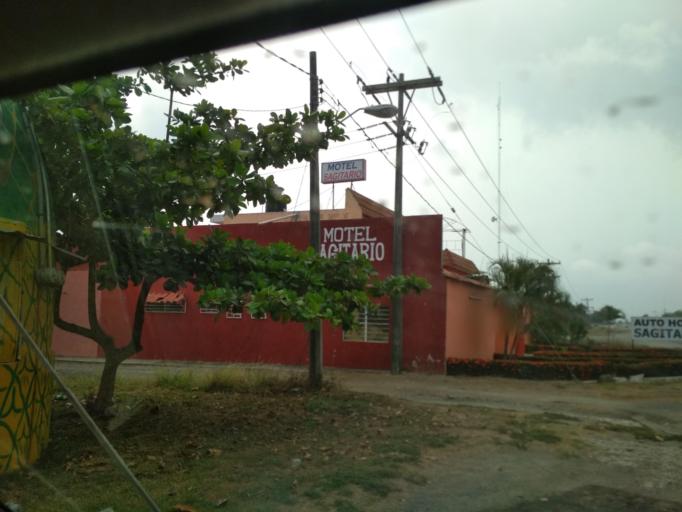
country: MX
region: Veracruz
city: Paso del Toro
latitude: 19.0088
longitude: -96.1160
